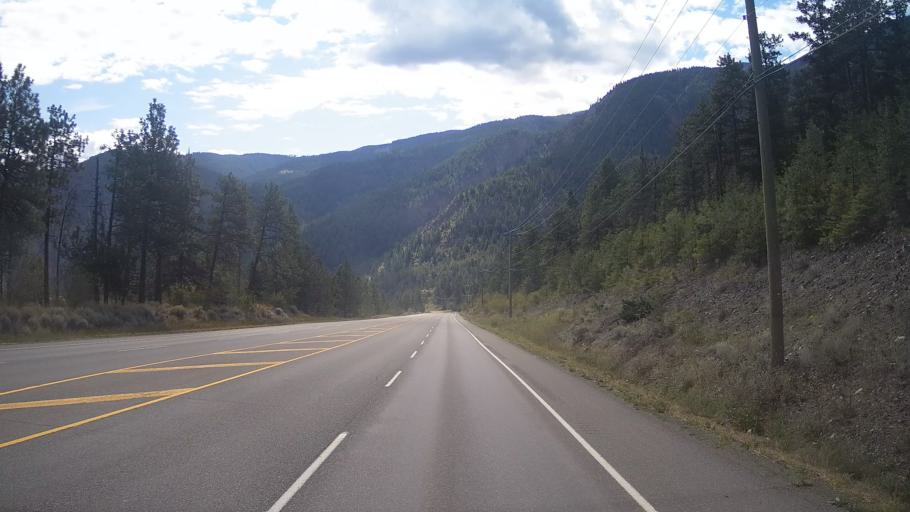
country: CA
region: British Columbia
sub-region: Thompson-Nicola Regional District
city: Ashcroft
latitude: 50.2525
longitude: -121.5070
